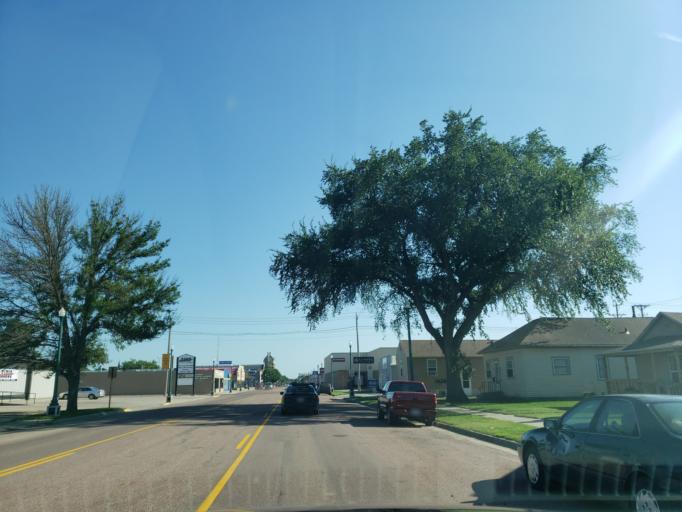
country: US
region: South Dakota
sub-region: Davison County
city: Mitchell
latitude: 43.7186
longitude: -98.0257
